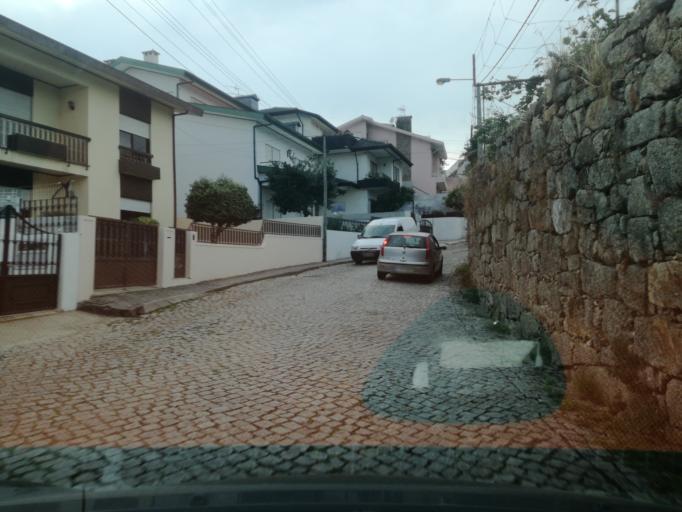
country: PT
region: Porto
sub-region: Maia
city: Maia
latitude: 41.2445
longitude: -8.6046
